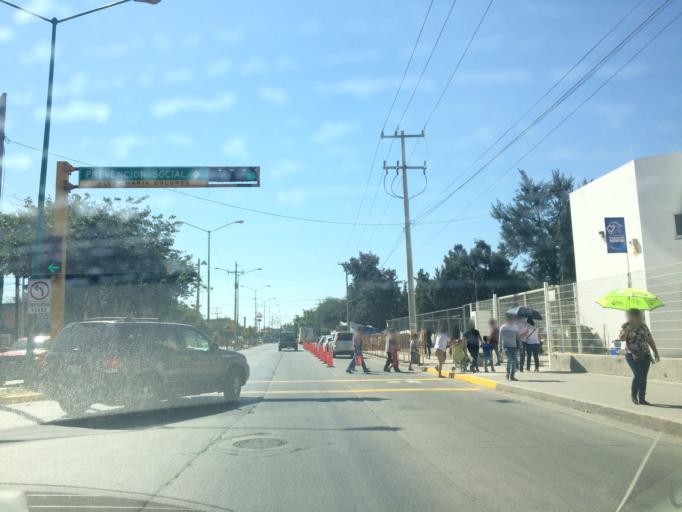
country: MX
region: Guanajuato
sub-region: Leon
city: San Jose de Duran (Los Troncoso)
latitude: 21.0955
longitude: -101.6639
